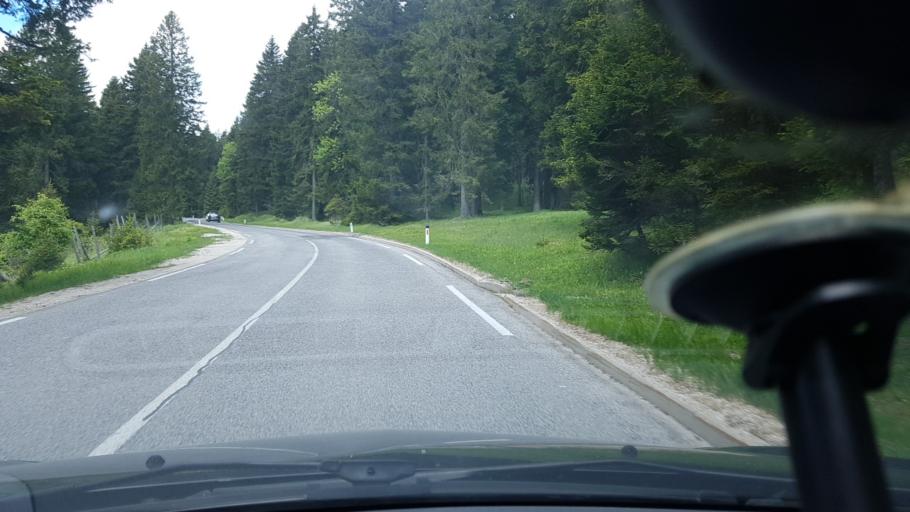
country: SI
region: Mislinja
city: Mislinja
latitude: 46.4491
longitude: 15.3251
